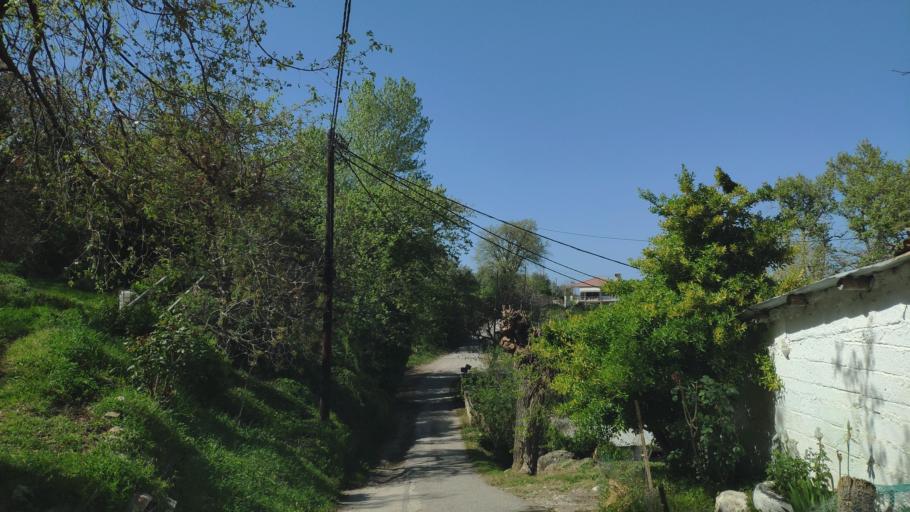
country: GR
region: West Greece
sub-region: Nomos Achaias
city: Aiyira
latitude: 38.0789
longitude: 22.3379
